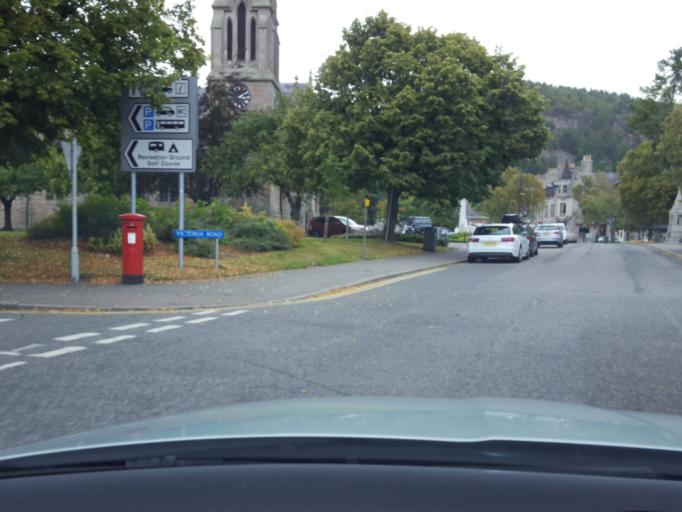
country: GB
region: Scotland
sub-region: Aberdeenshire
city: Ballater
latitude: 57.0484
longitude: -3.0392
